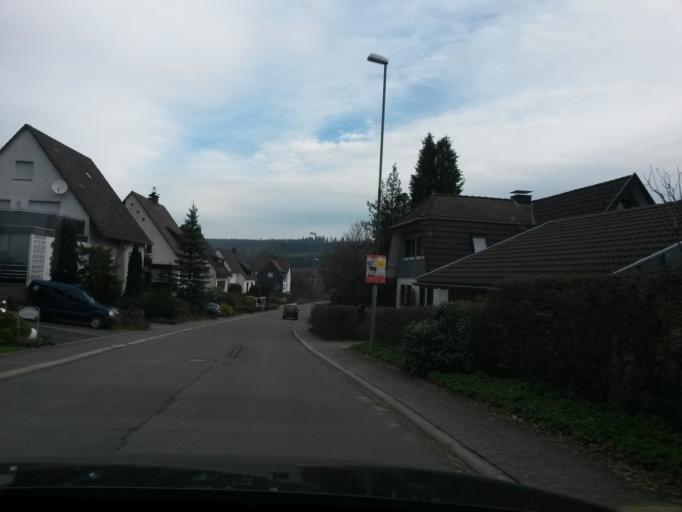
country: DE
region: North Rhine-Westphalia
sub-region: Regierungsbezirk Arnsberg
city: Herscheid
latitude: 51.1761
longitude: 7.7381
